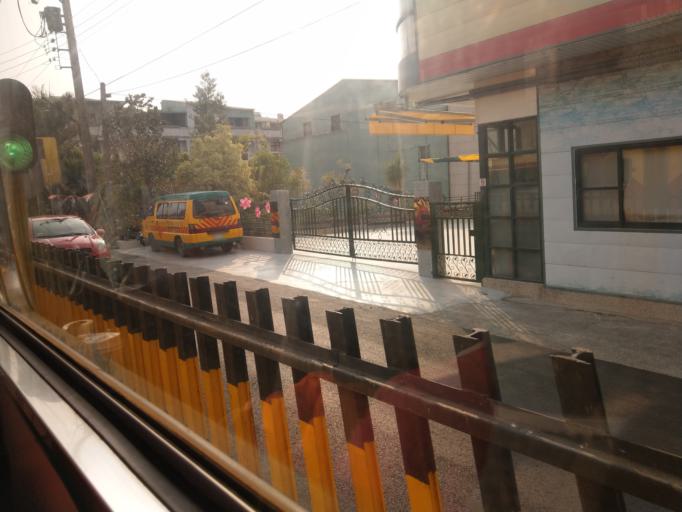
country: TW
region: Taiwan
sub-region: Chiayi
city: Jiayi Shi
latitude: 23.5226
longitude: 120.5496
